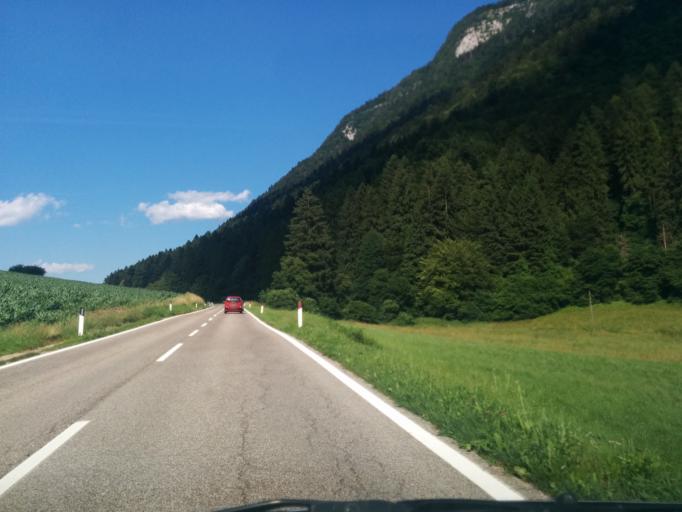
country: IT
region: Trentino-Alto Adige
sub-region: Provincia di Trento
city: Fiave
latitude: 45.9700
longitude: 10.8142
